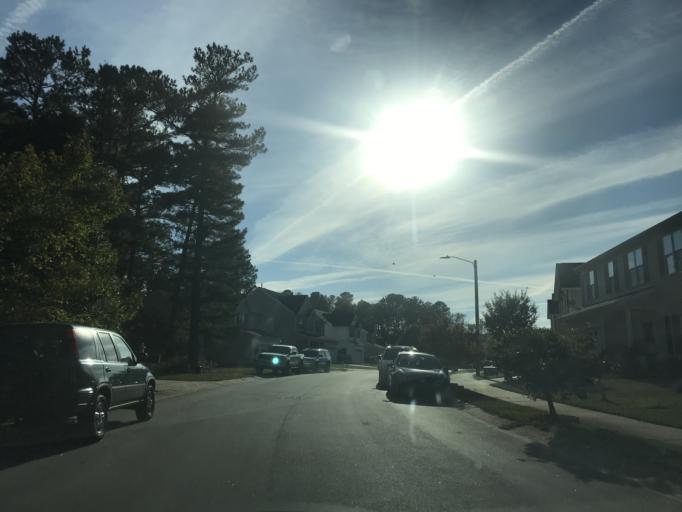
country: US
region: North Carolina
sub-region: Wake County
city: Wake Forest
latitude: 35.8949
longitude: -78.5457
